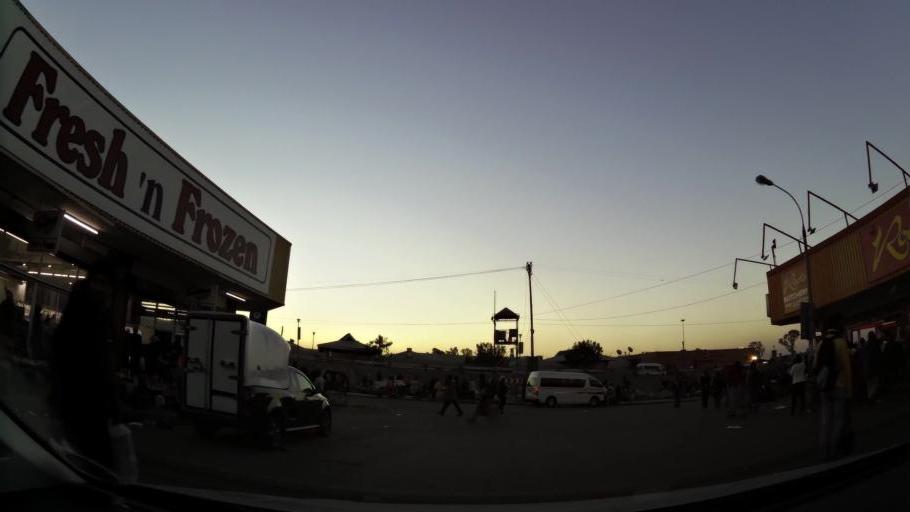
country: ZA
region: North-West
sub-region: Bojanala Platinum District Municipality
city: Rustenburg
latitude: -25.6631
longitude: 27.2374
